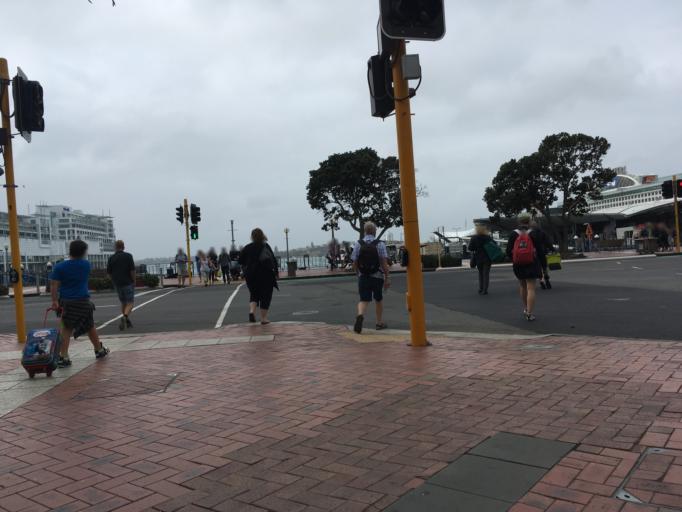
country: NZ
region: Auckland
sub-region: Auckland
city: Auckland
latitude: -36.8431
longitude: 174.7657
